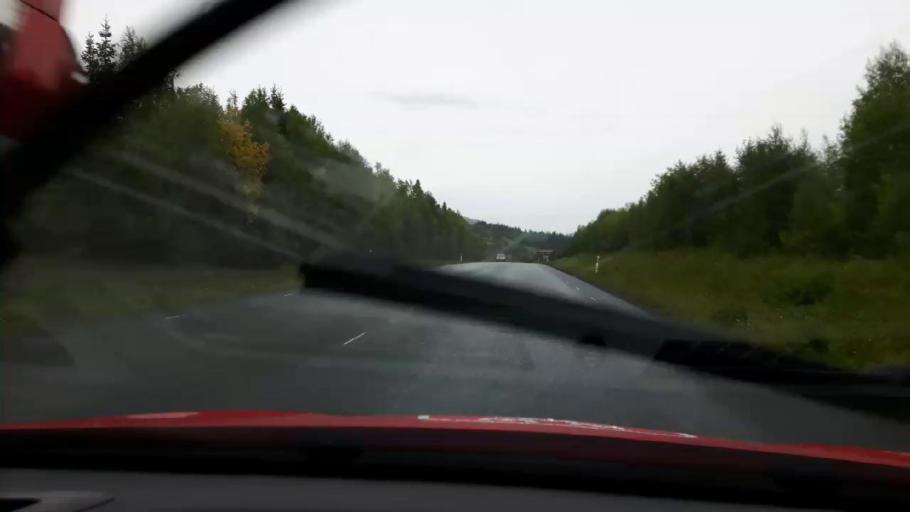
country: SE
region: Jaemtland
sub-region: Are Kommun
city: Are
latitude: 63.3951
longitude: 12.8960
